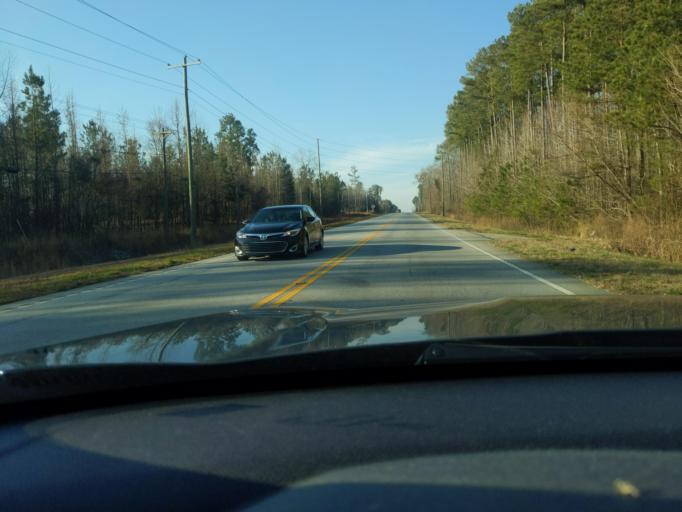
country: US
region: South Carolina
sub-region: Newberry County
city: Newberry
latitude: 34.2410
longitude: -81.6484
